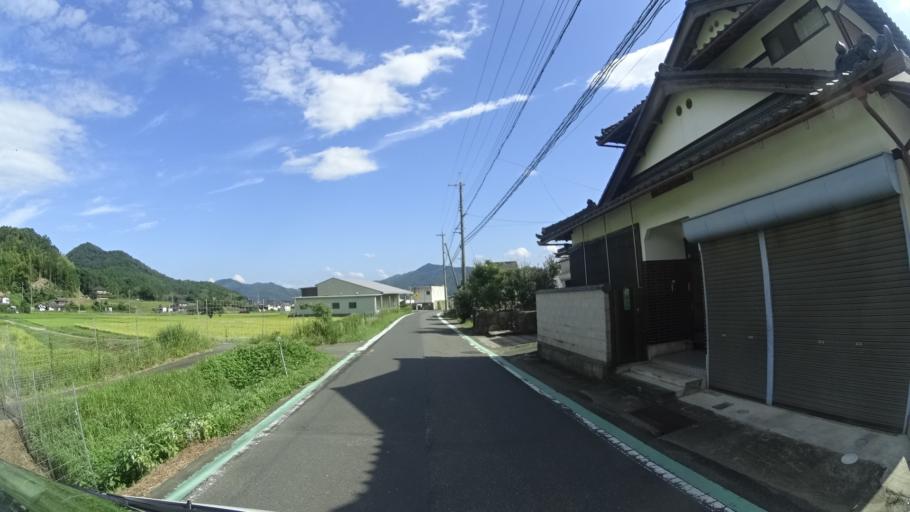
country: JP
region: Kyoto
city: Fukuchiyama
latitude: 35.3217
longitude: 135.1805
